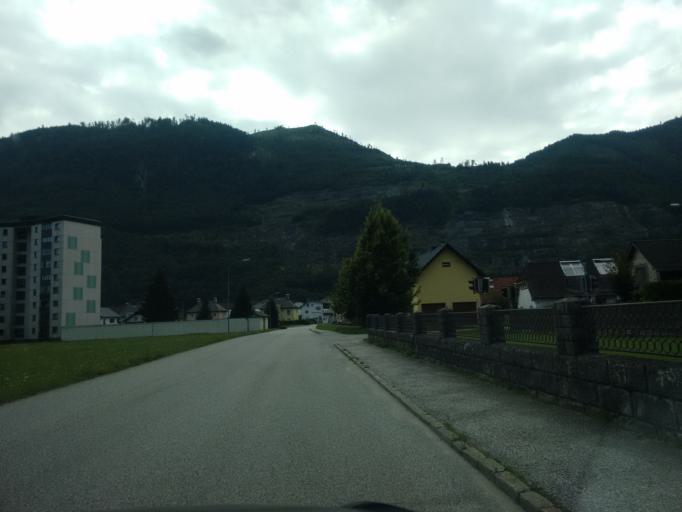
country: AT
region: Upper Austria
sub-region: Politischer Bezirk Gmunden
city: Ebensee
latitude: 47.8005
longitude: 13.7712
